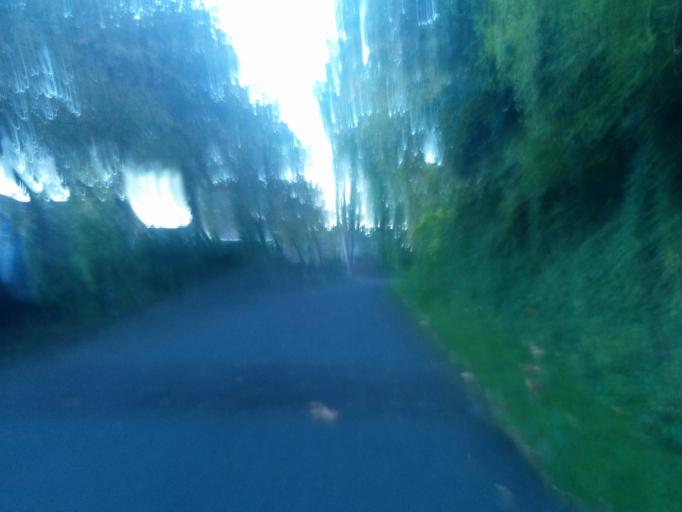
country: US
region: Washington
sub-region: King County
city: Lake Forest Park
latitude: 47.7190
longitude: -122.2795
